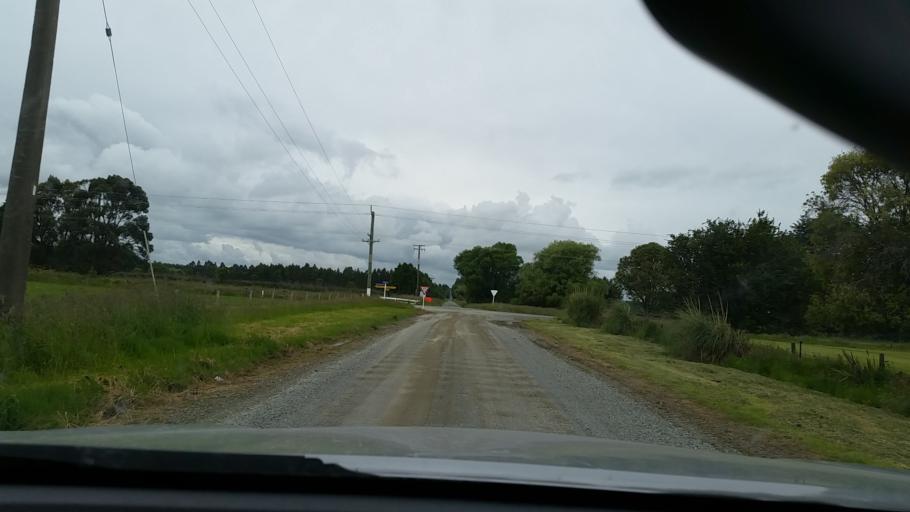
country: NZ
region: Southland
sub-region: Southland District
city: Winton
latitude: -46.1837
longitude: 168.3016
